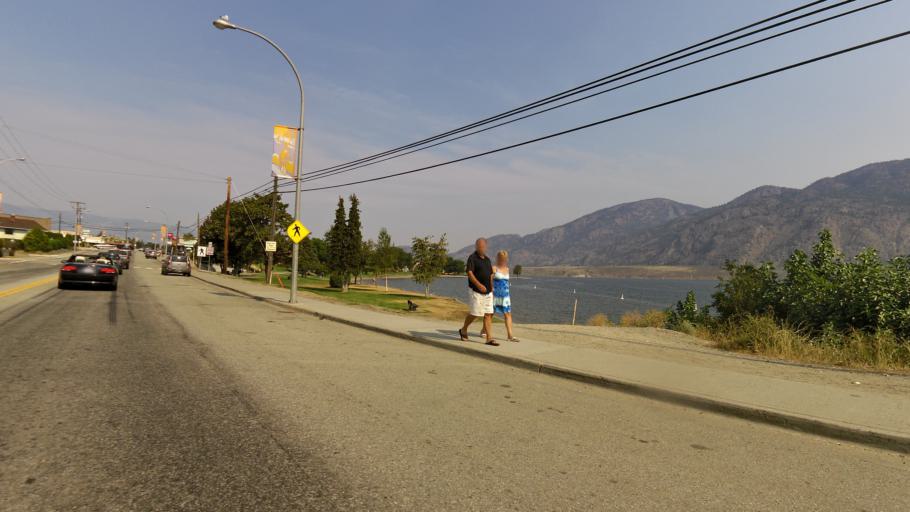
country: CA
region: British Columbia
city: Osoyoos
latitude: 49.0287
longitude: -119.4604
